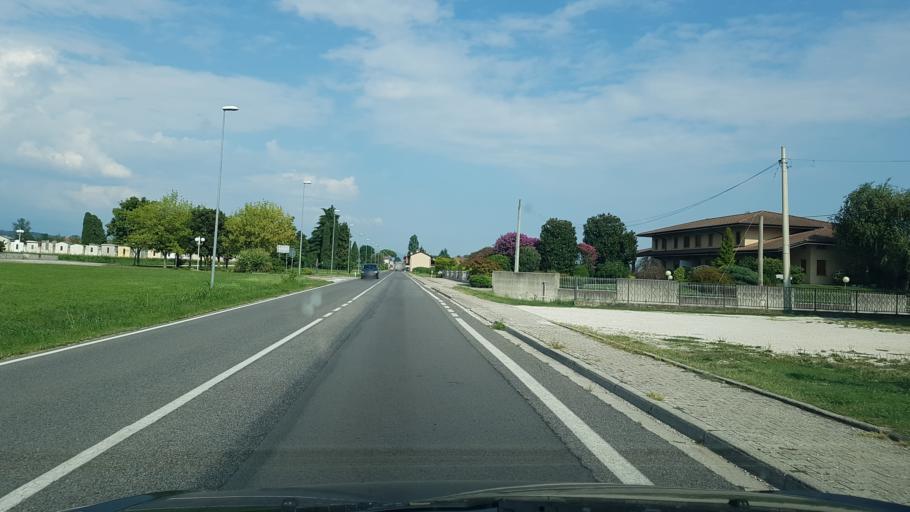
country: IT
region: Friuli Venezia Giulia
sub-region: Provincia di Udine
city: San Vito di Fagagna
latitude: 46.0881
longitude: 13.0568
